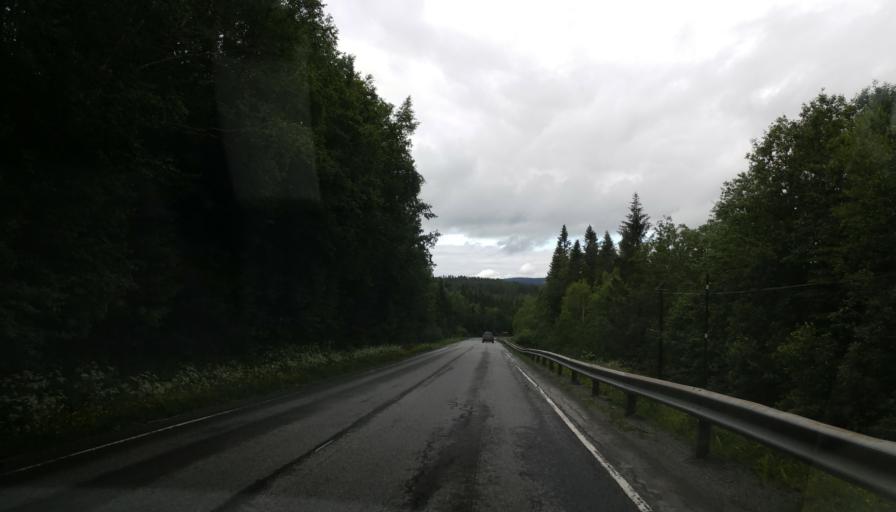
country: NO
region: Sor-Trondelag
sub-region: Selbu
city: Mebonden
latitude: 63.3679
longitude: 11.0738
